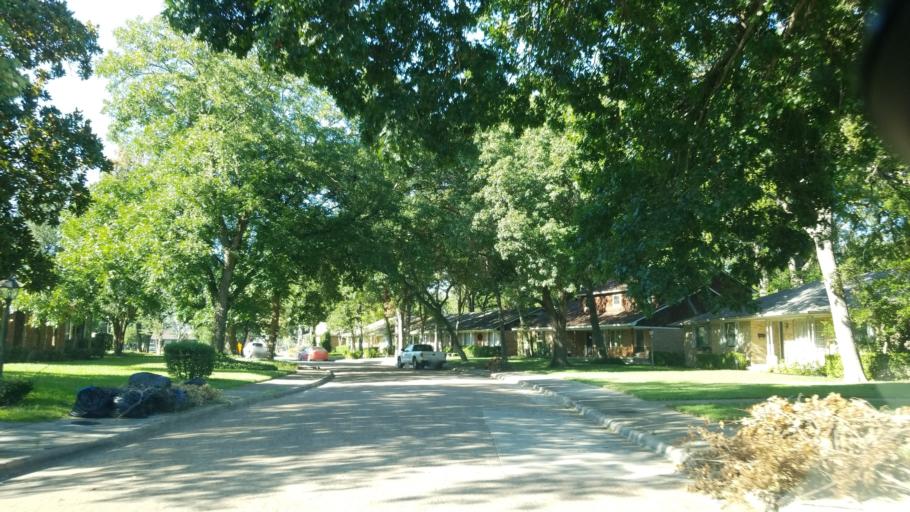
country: US
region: Texas
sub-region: Dallas County
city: Highland Park
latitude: 32.7892
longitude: -96.7062
